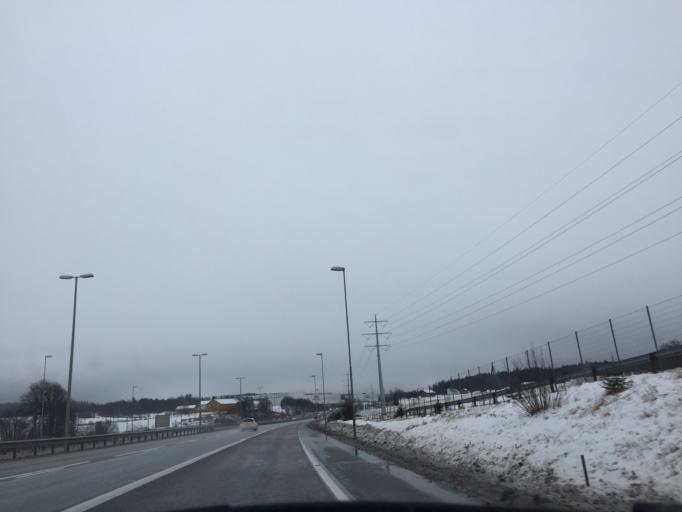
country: NO
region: Akershus
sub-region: Vestby
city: Vestby
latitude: 59.6018
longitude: 10.7379
